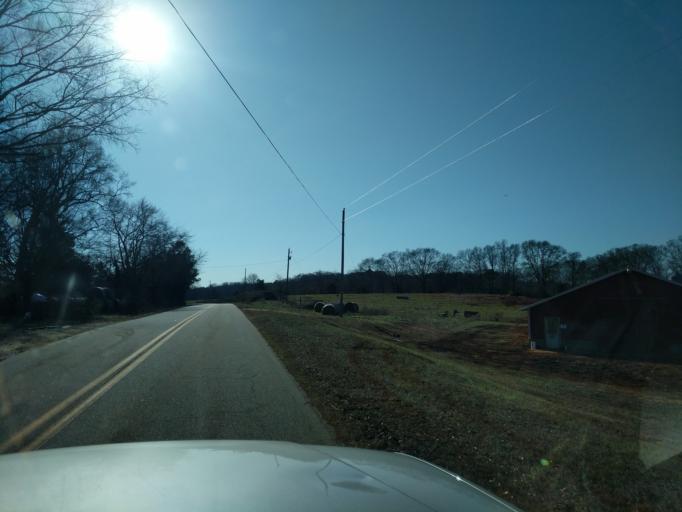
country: US
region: Georgia
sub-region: Hart County
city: Hartwell
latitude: 34.3410
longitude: -82.8592
